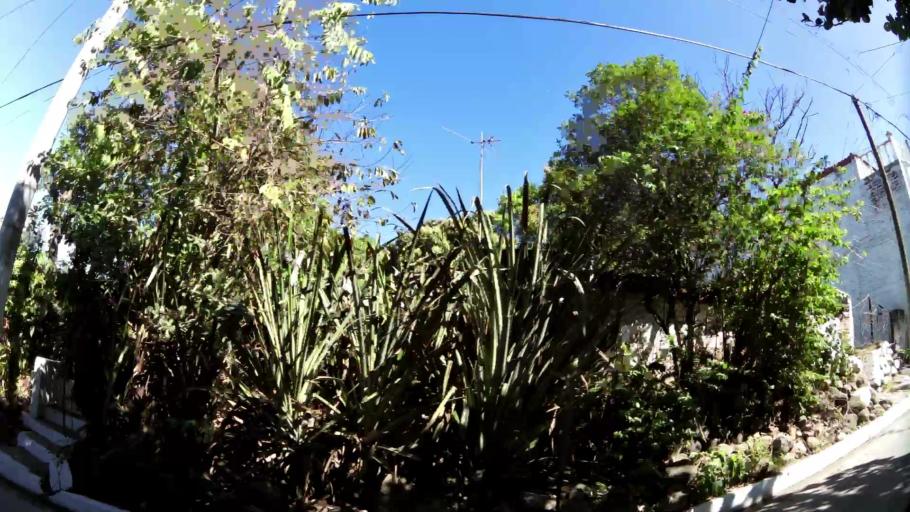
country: SV
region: La Libertad
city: San Juan Opico
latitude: 13.8753
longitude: -89.3545
